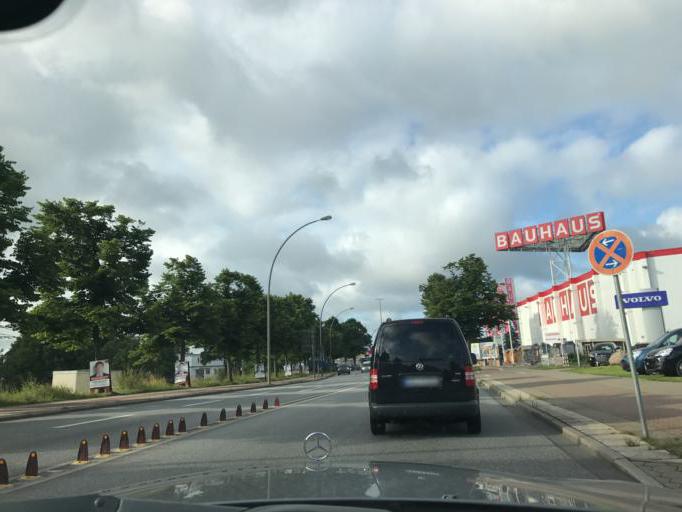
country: DE
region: Hamburg
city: Bergedorf
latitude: 53.4839
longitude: 10.2092
